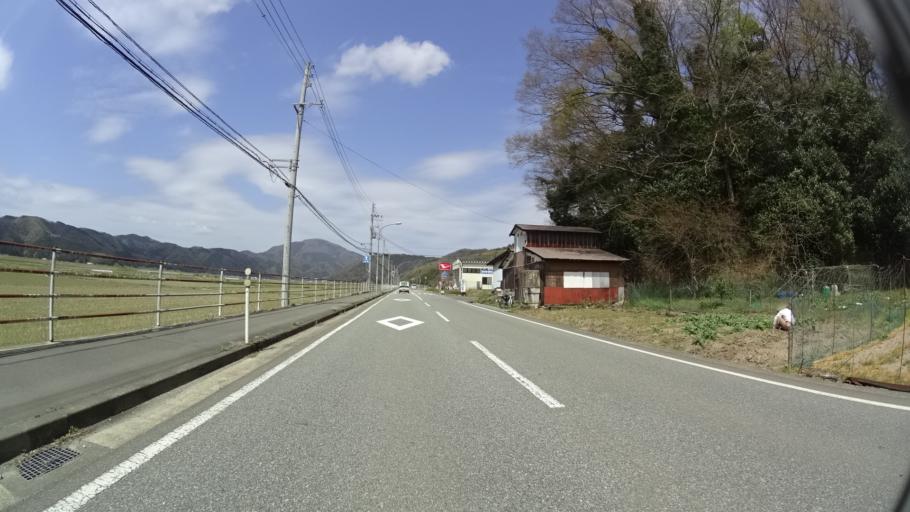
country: JP
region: Hyogo
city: Toyooka
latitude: 35.5673
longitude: 134.8190
